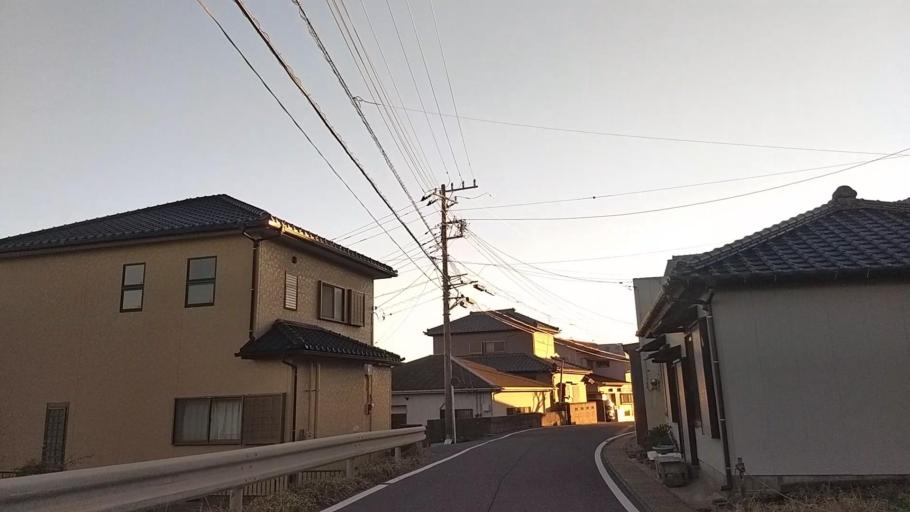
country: JP
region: Chiba
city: Hasaki
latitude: 35.6964
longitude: 140.8621
